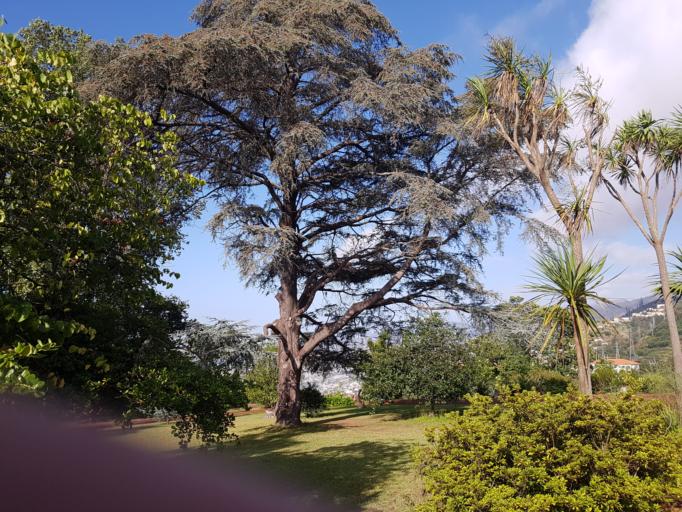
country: PT
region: Madeira
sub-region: Santa Cruz
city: Camacha
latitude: 32.6594
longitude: -16.8675
